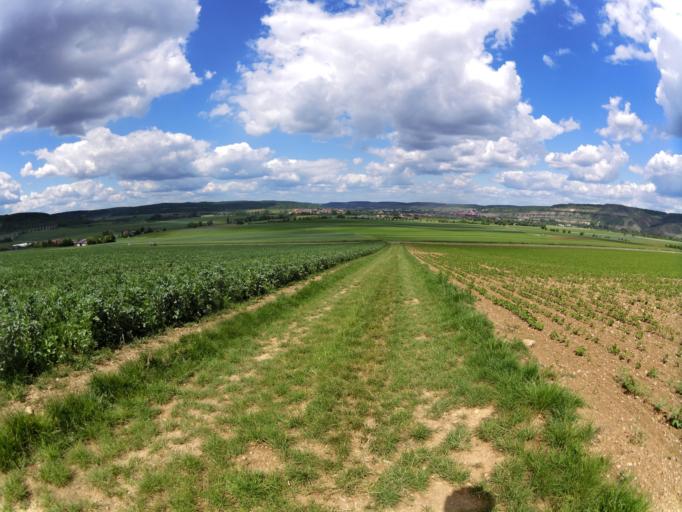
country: DE
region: Bavaria
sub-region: Regierungsbezirk Unterfranken
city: Zellingen
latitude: 49.8742
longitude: 9.8134
